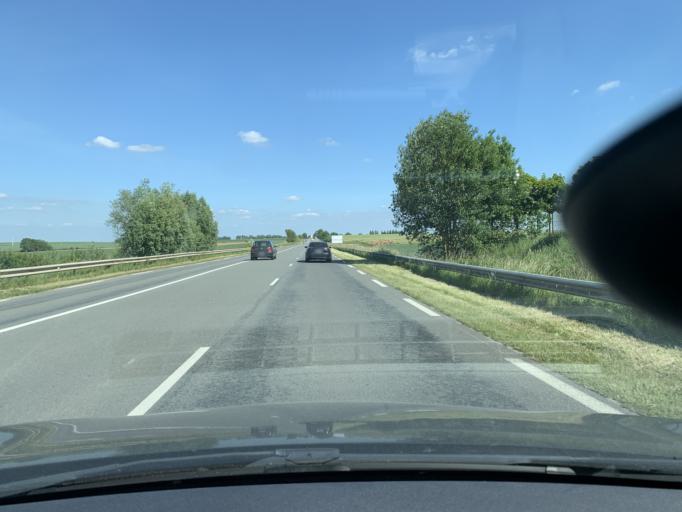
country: FR
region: Nord-Pas-de-Calais
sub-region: Departement du Nord
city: Caudry
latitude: 50.1296
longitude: 3.4309
